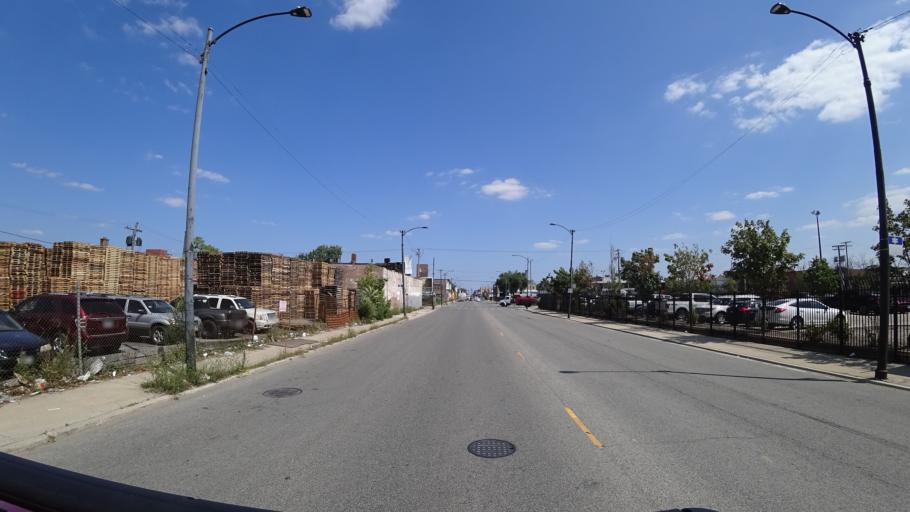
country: US
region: Illinois
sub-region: Cook County
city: Cicero
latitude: 41.8660
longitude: -87.7383
